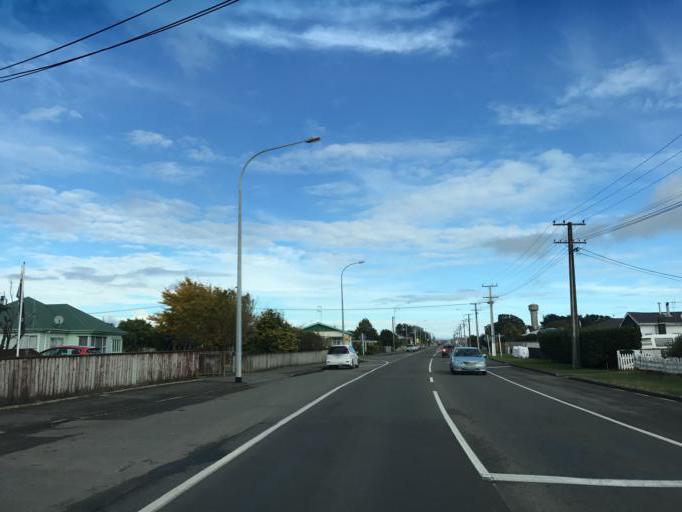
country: NZ
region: Manawatu-Wanganui
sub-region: Horowhenua District
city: Foxton
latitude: -40.4732
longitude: 175.2857
